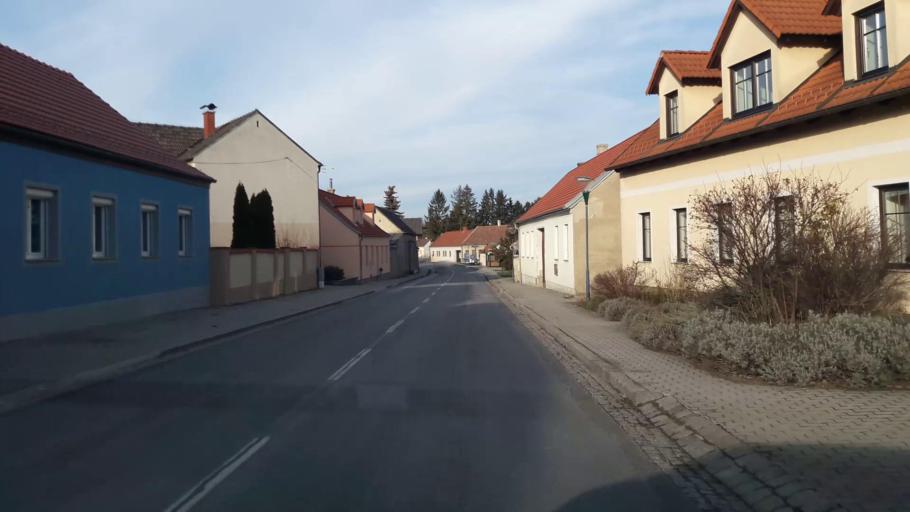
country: AT
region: Lower Austria
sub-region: Politischer Bezirk Ganserndorf
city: Bad Pirawarth
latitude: 48.4479
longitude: 16.6039
